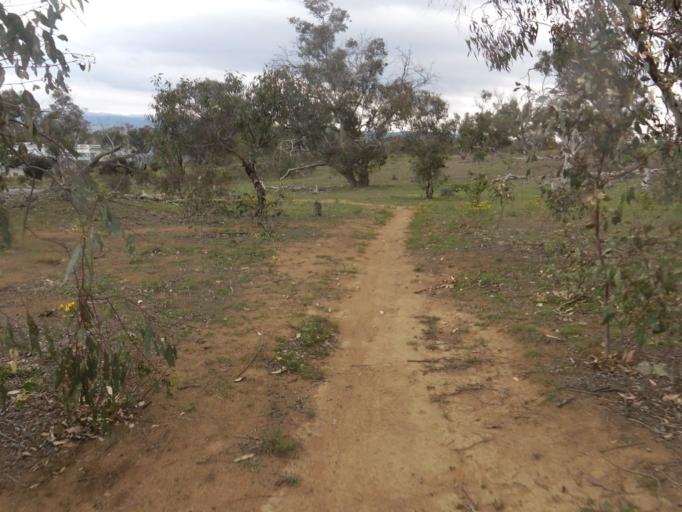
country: AU
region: Australian Capital Territory
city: Forrest
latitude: -35.3464
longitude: 149.1351
